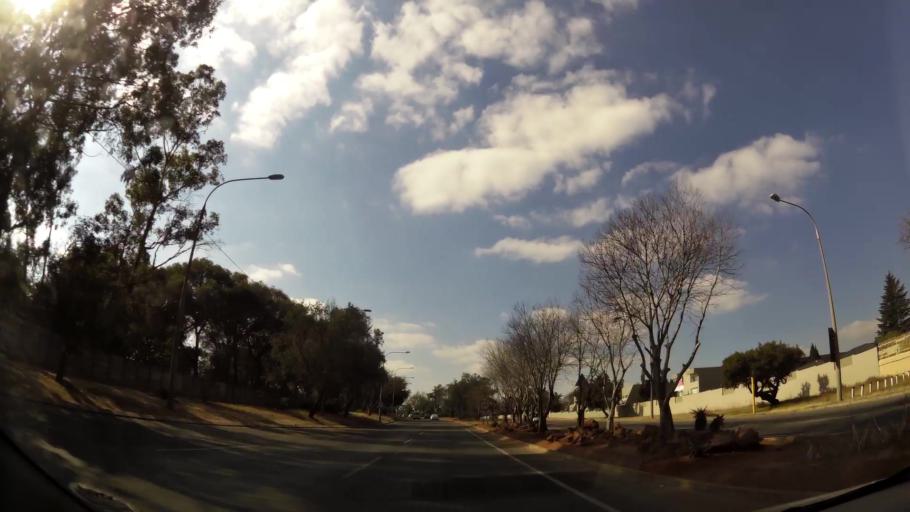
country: ZA
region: Gauteng
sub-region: West Rand District Municipality
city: Krugersdorp
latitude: -26.0870
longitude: 27.7858
